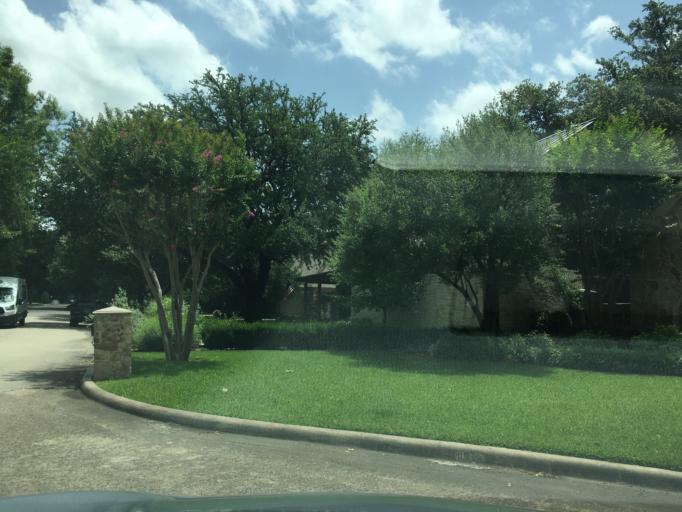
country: US
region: Texas
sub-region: Dallas County
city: University Park
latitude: 32.8915
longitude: -96.7990
